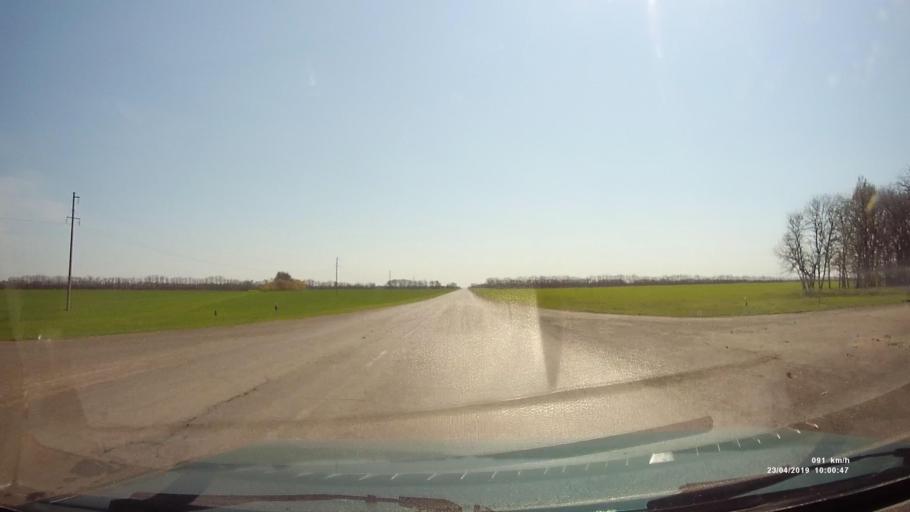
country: RU
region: Rostov
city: Sovetskoye
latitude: 46.7688
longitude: 42.1381
